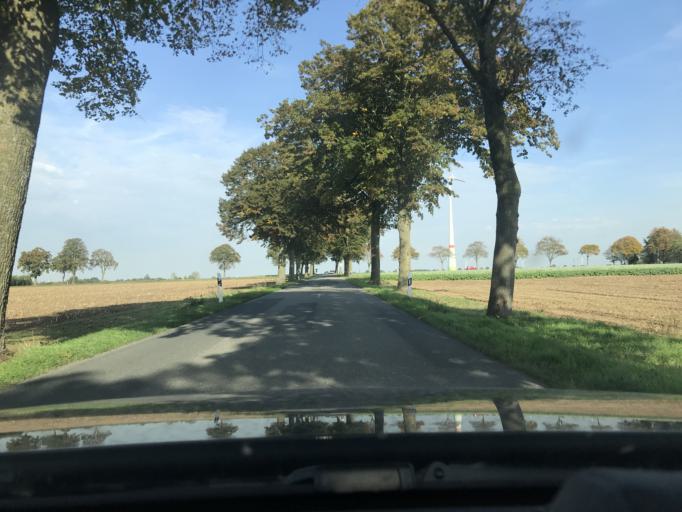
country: DE
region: North Rhine-Westphalia
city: Kalkar
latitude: 51.7149
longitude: 6.2699
